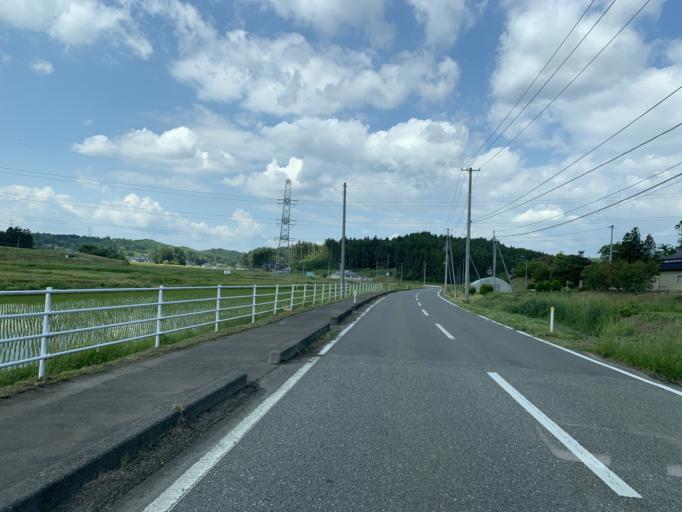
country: JP
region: Iwate
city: Ichinoseki
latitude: 38.7910
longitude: 140.9681
